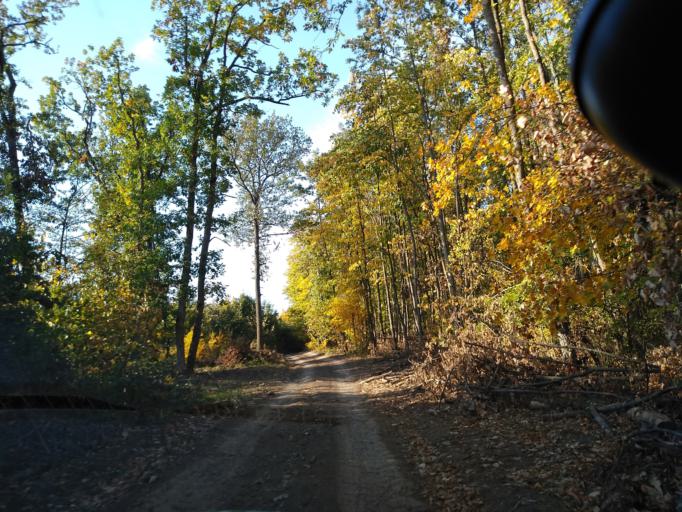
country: RO
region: Timis
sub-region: Comuna Bogda
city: Bogda
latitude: 45.9246
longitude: 21.6209
